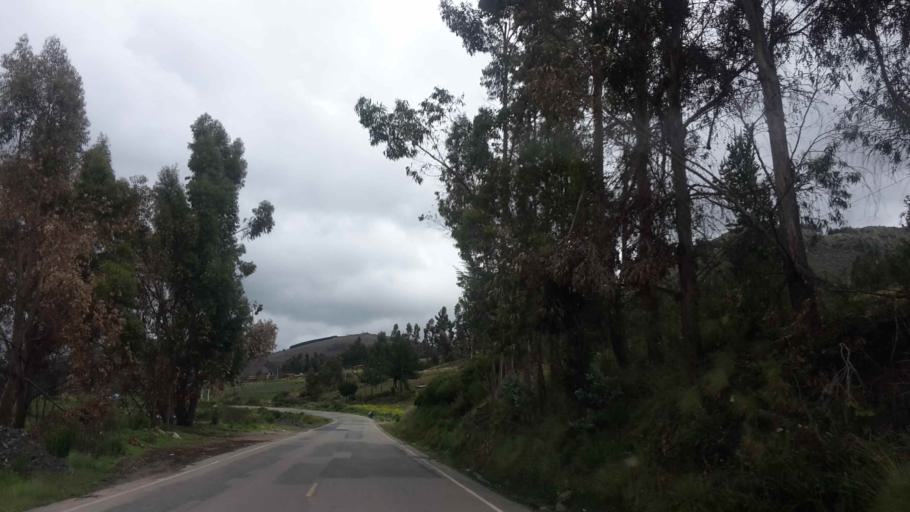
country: BO
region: Cochabamba
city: Arani
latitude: -17.4819
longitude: -65.5682
